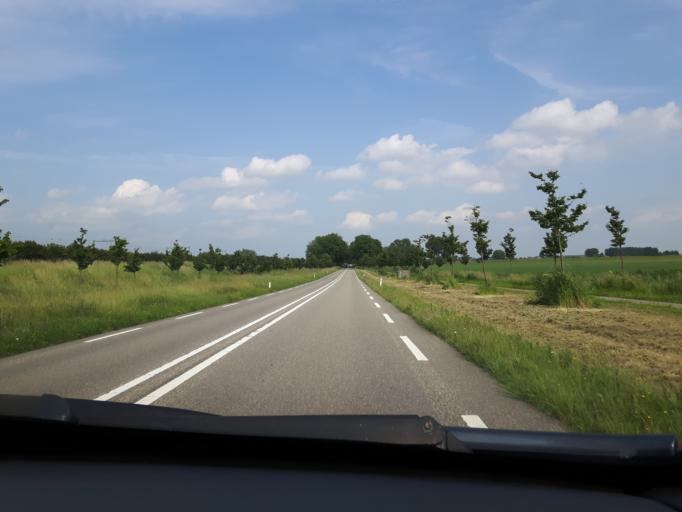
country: NL
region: Zeeland
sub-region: Gemeente Veere
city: Veere
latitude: 51.5024
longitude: 3.7105
